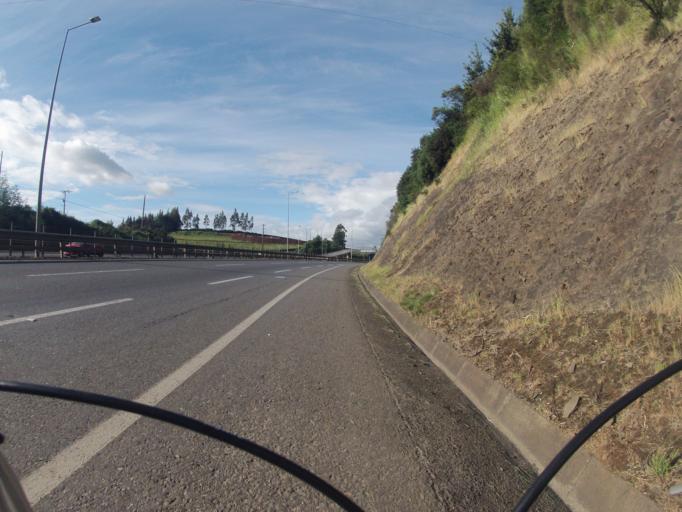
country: CL
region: Araucania
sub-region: Provincia de Cautin
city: Temuco
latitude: -38.8046
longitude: -72.6264
